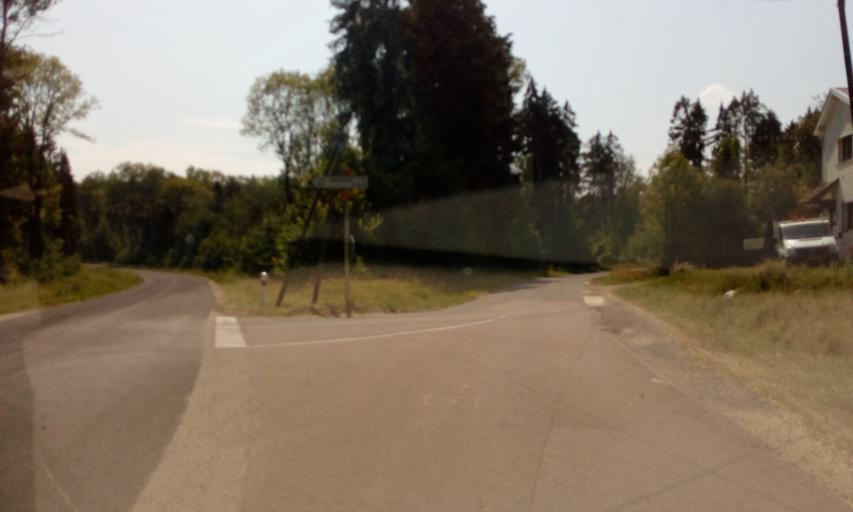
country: FR
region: Lorraine
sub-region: Departement de la Meuse
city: Belleville-sur-Meuse
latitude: 49.2726
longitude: 5.4786
